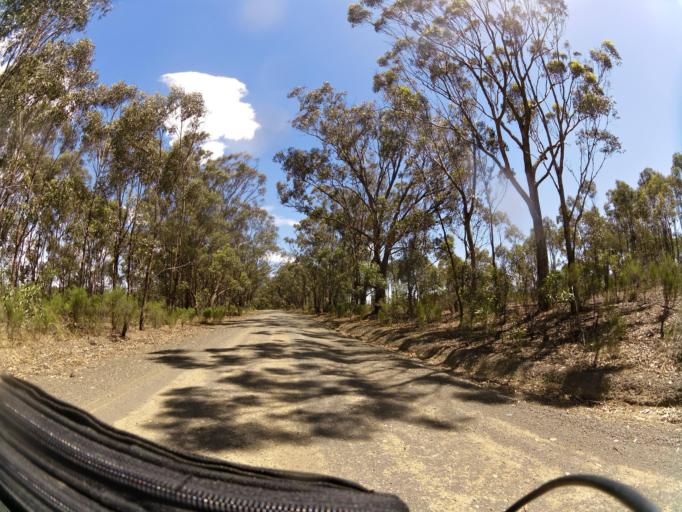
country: AU
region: Victoria
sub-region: Campaspe
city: Kyabram
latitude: -36.7969
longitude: 145.0807
